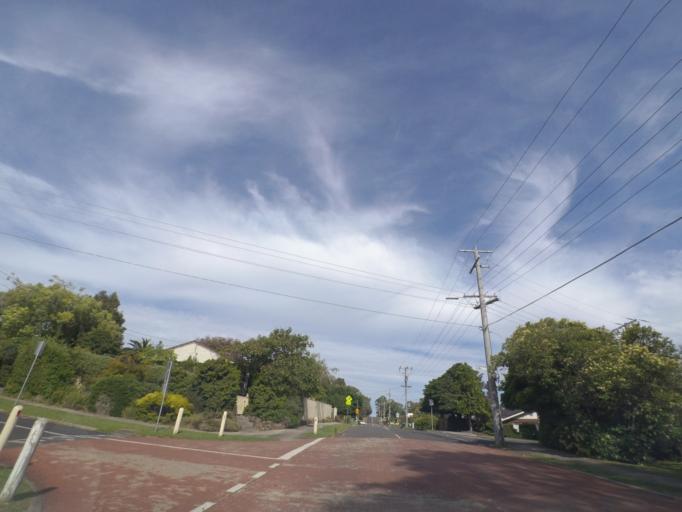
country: AU
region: Victoria
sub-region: Banyule
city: Viewbank
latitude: -37.7330
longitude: 145.0927
